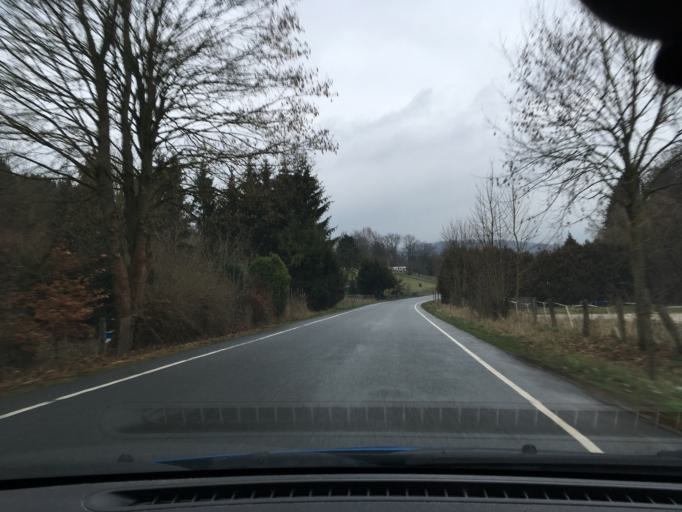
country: DE
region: Lower Saxony
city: Hardegsen
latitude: 51.6456
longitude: 9.8223
